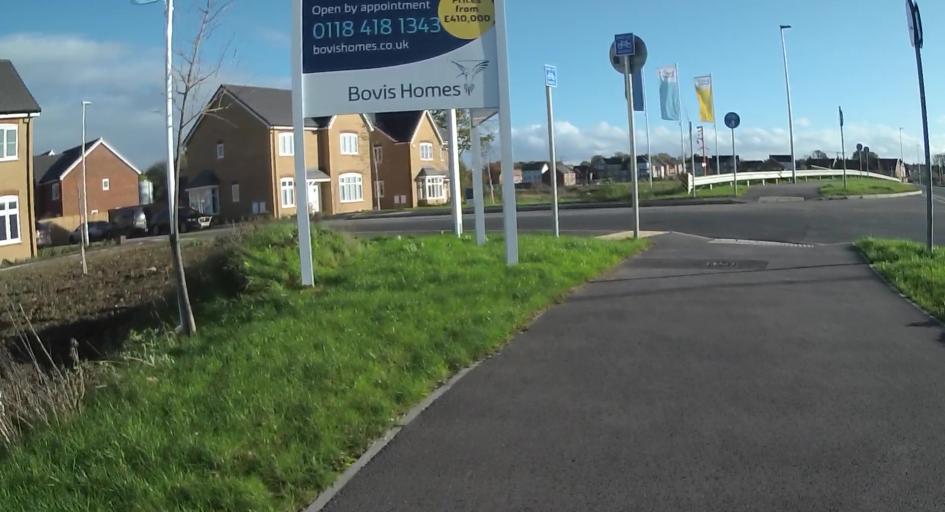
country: GB
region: England
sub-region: Wokingham
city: Winnersh
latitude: 51.4314
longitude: -0.8920
